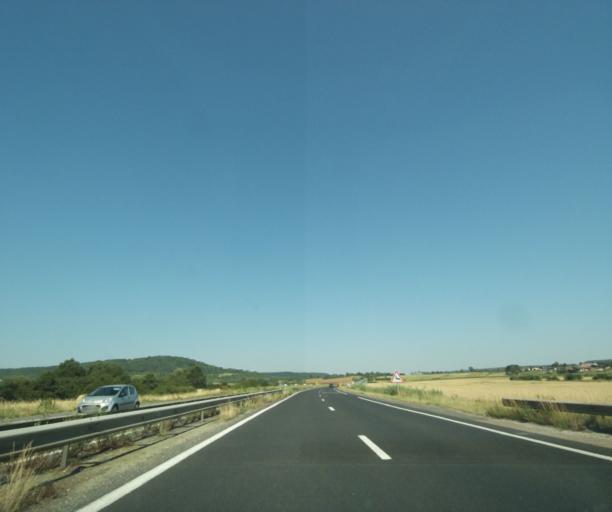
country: FR
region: Lorraine
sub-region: Departement de Meurthe-et-Moselle
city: Domgermain
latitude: 48.6460
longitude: 5.8512
